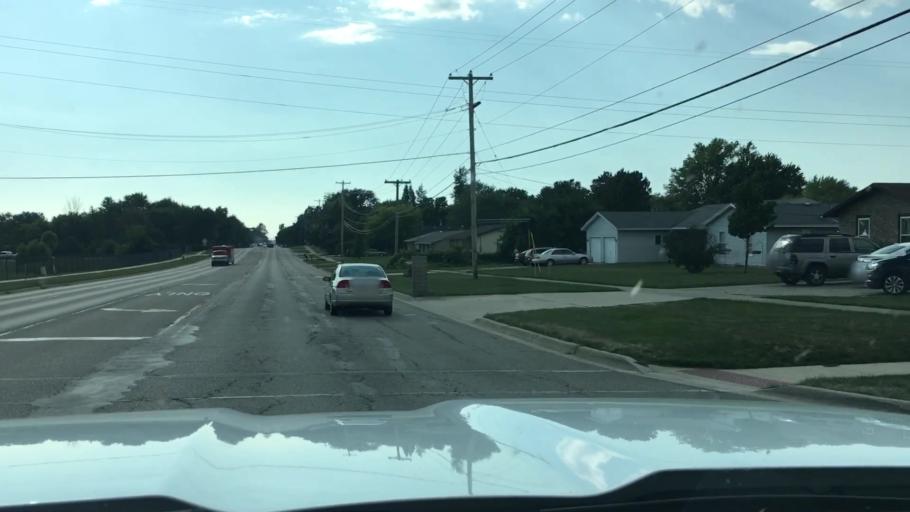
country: US
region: Michigan
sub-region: Kent County
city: Kentwood
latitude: 42.8547
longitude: -85.6144
